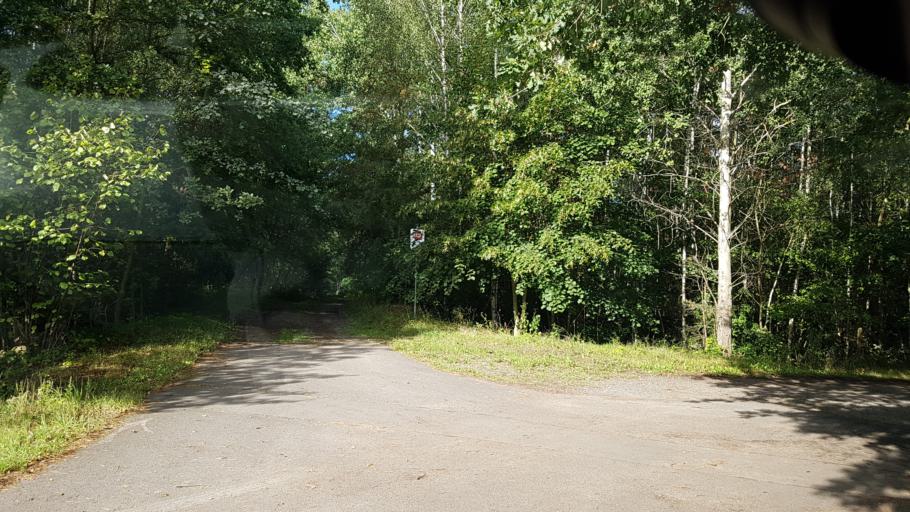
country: DE
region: Brandenburg
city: Tschernitz
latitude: 51.6368
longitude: 14.5888
